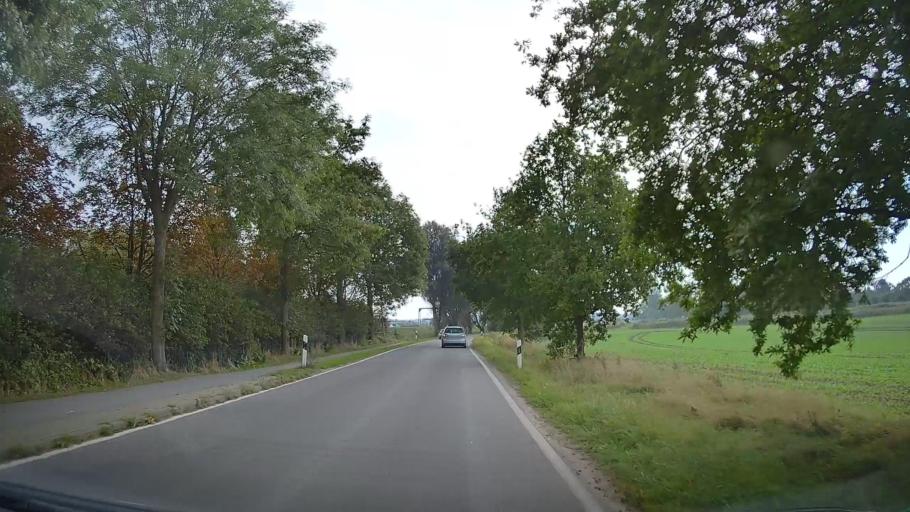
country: DE
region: Schleswig-Holstein
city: Blekendorf
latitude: 54.3381
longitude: 10.6441
